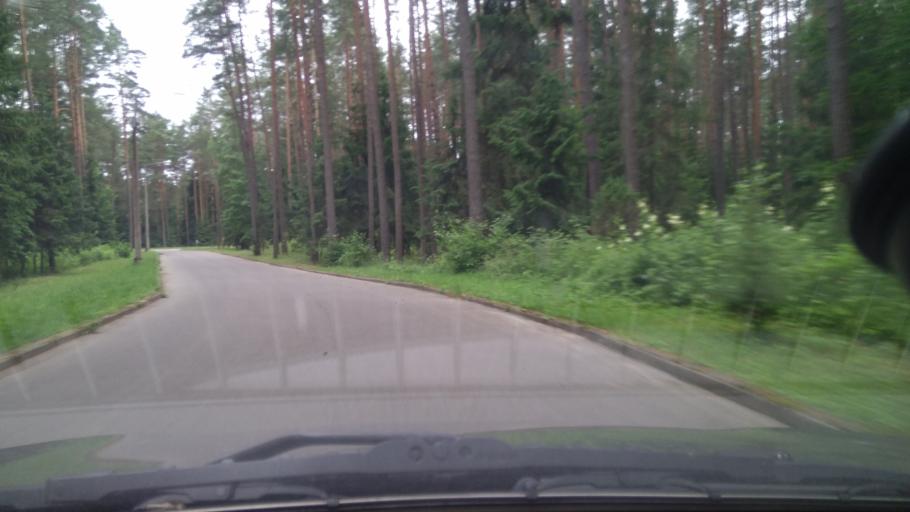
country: BY
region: Minsk
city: Rakaw
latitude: 53.9794
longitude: 27.0135
